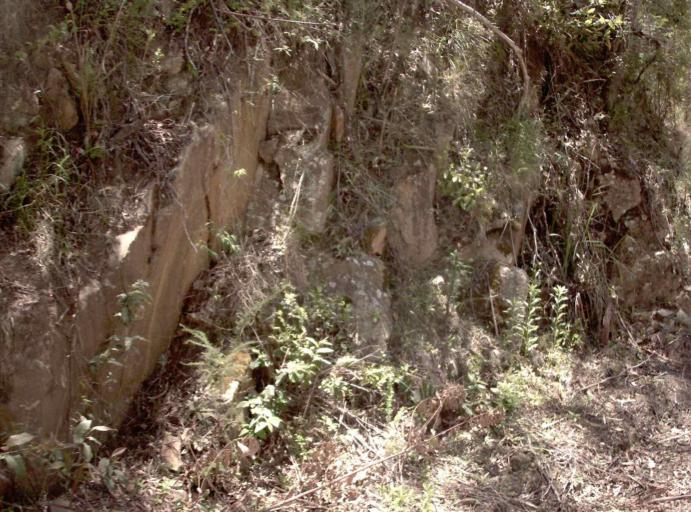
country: AU
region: New South Wales
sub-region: Bombala
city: Bombala
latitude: -37.4572
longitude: 148.9363
